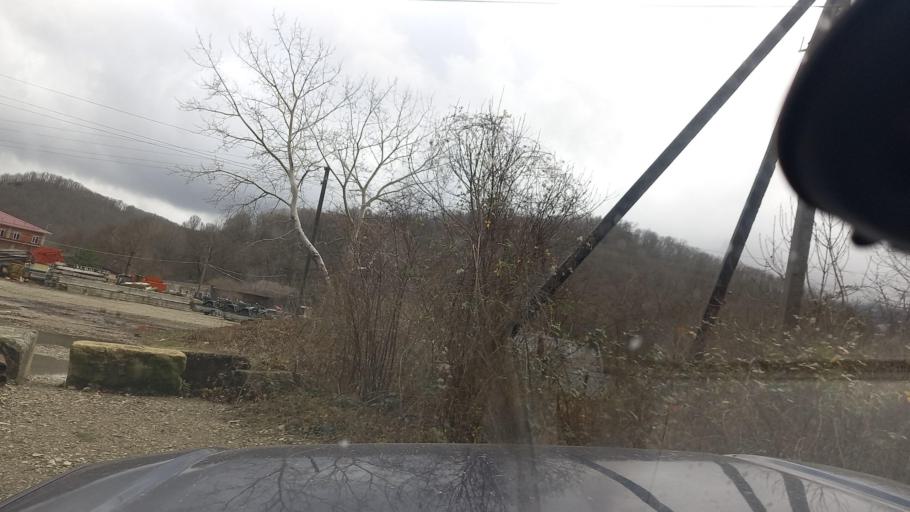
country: RU
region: Krasnodarskiy
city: Pshada
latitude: 44.4816
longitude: 38.4044
